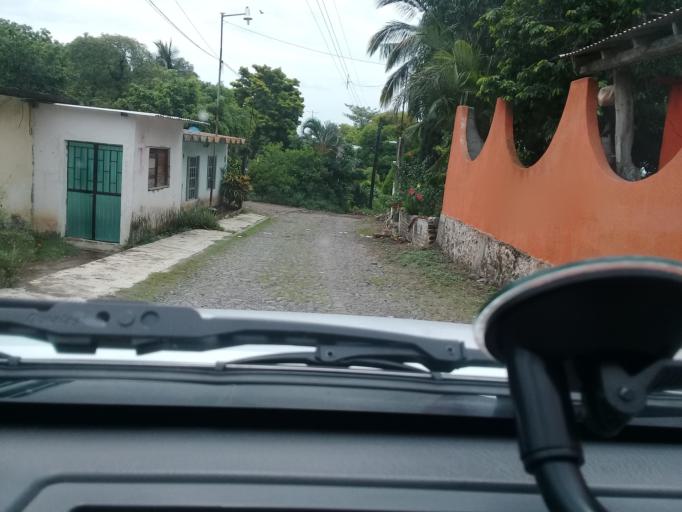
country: MX
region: Veracruz
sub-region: Paso de Ovejas
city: El Hatito
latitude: 19.2800
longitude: -96.3892
